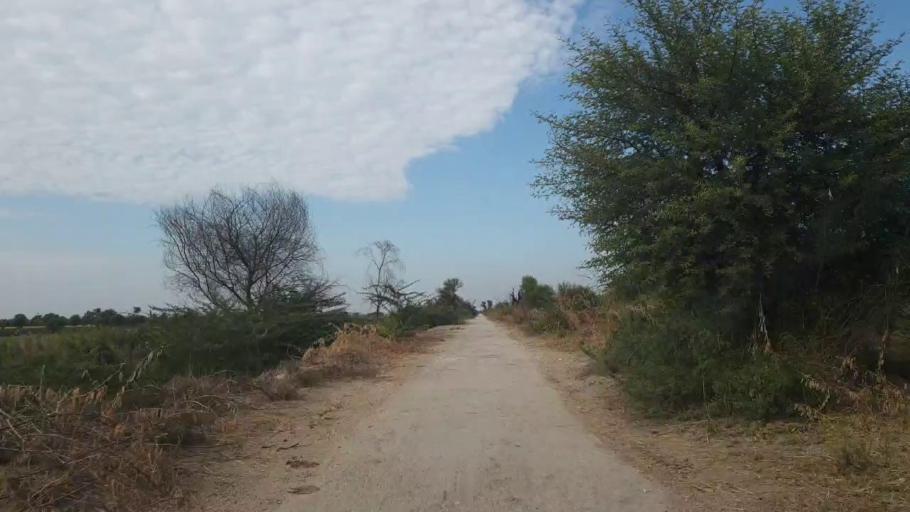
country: PK
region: Sindh
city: Sinjhoro
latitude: 26.0498
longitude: 68.8757
